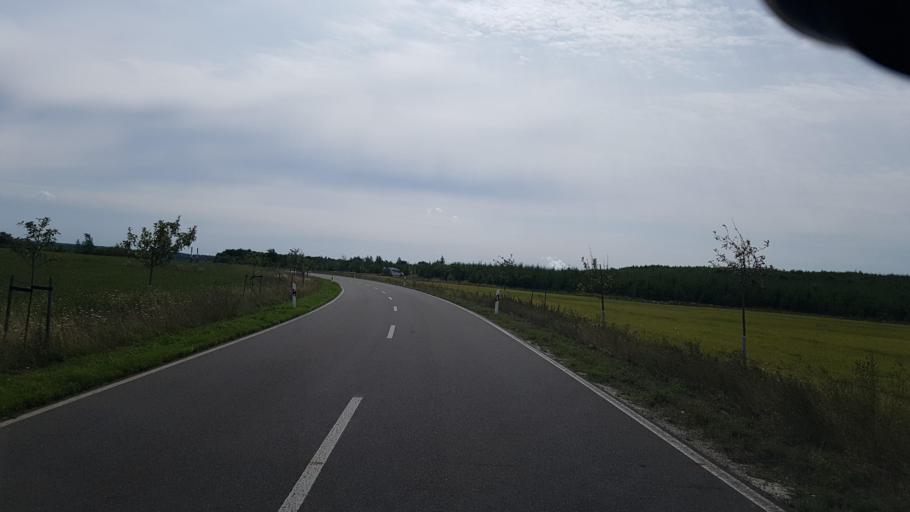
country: DE
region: Brandenburg
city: Drebkau
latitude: 51.6146
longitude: 14.2598
